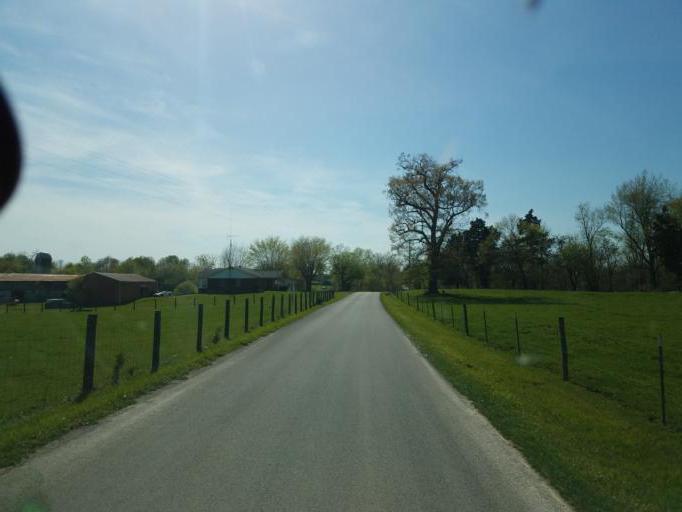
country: US
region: Kentucky
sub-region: Edmonson County
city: Brownsville
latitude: 37.1221
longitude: -86.1480
